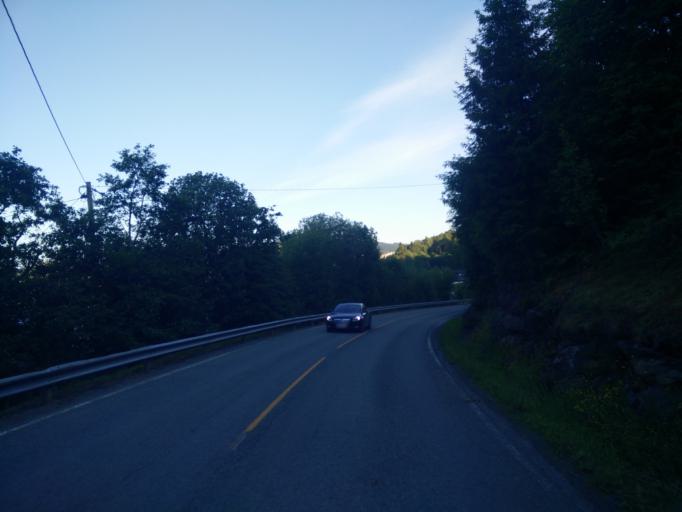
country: NO
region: Sor-Trondelag
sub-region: Skaun
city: Borsa
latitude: 63.3415
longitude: 10.0568
